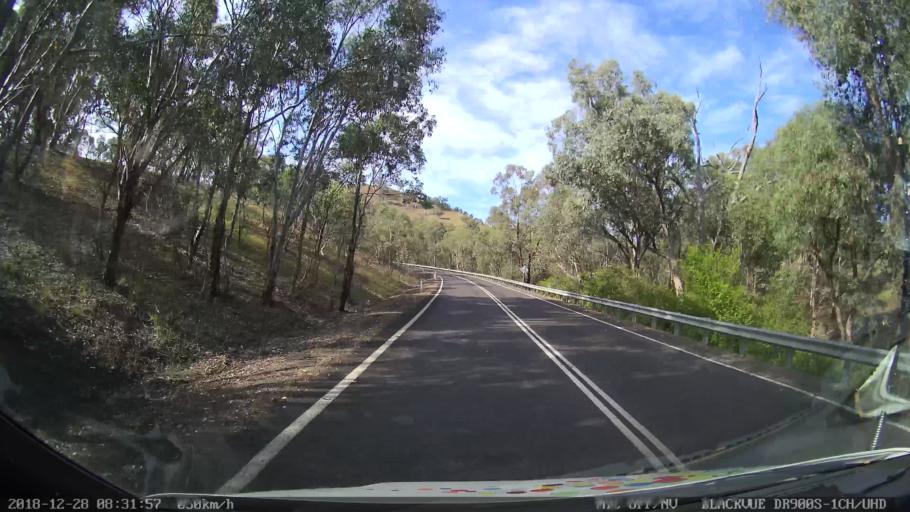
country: AU
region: New South Wales
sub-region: Blayney
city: Blayney
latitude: -33.9617
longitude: 149.3154
